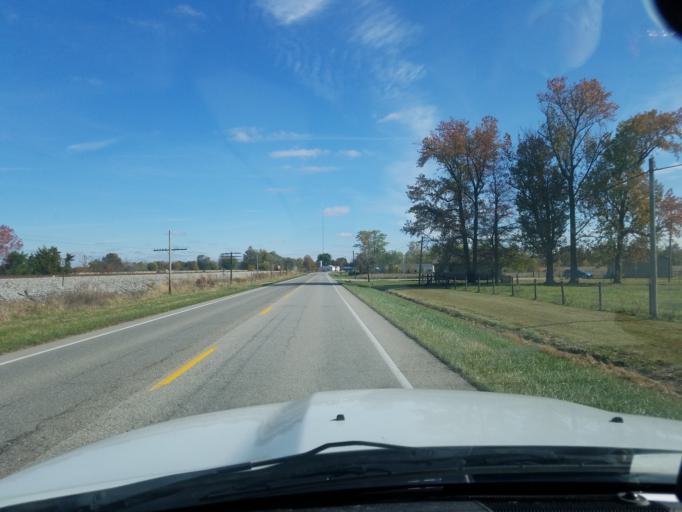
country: US
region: Indiana
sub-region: Jennings County
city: North Vernon
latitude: 39.0317
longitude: -85.5203
